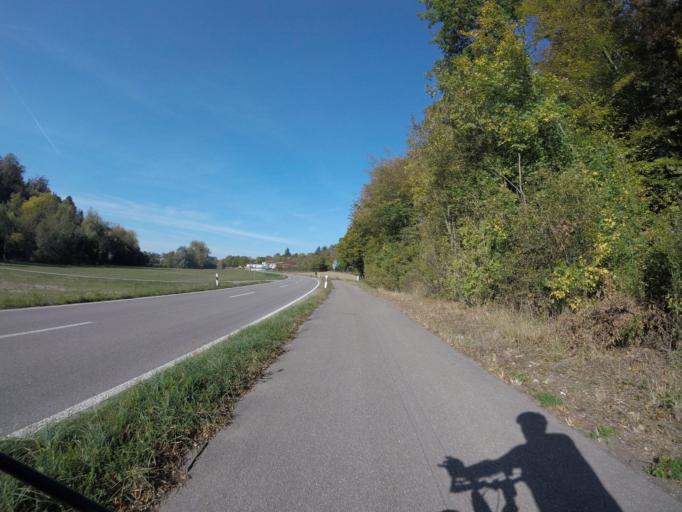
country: DE
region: Baden-Wuerttemberg
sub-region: Karlsruhe Region
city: Bretten
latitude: 49.0211
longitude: 8.7169
